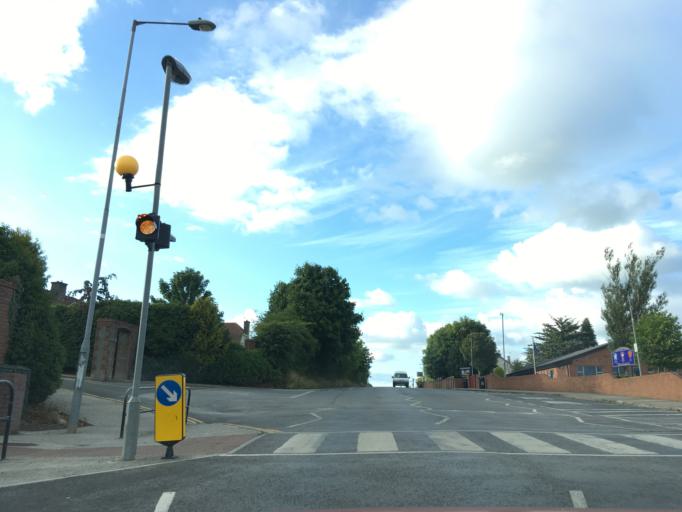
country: IE
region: Munster
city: Cashel
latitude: 52.5095
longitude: -7.8858
